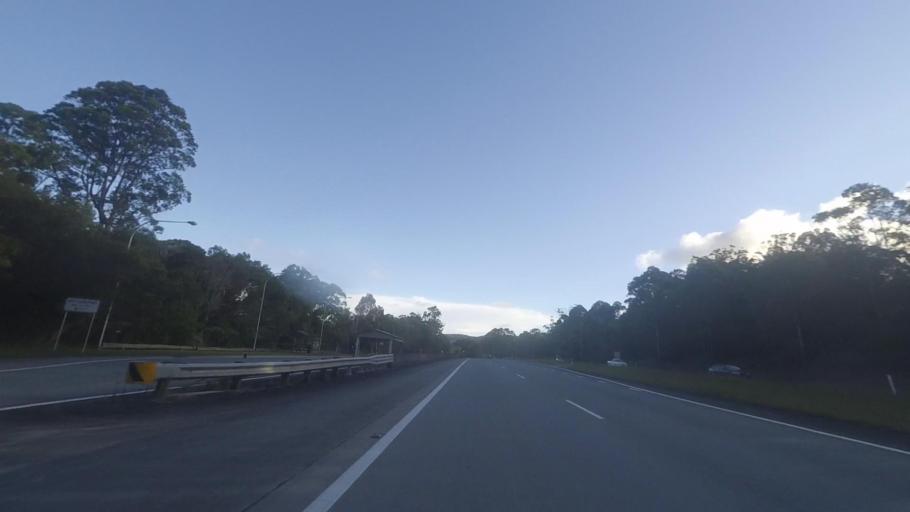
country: AU
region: New South Wales
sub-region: Great Lakes
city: Nabiac
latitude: -32.2508
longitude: 152.3232
